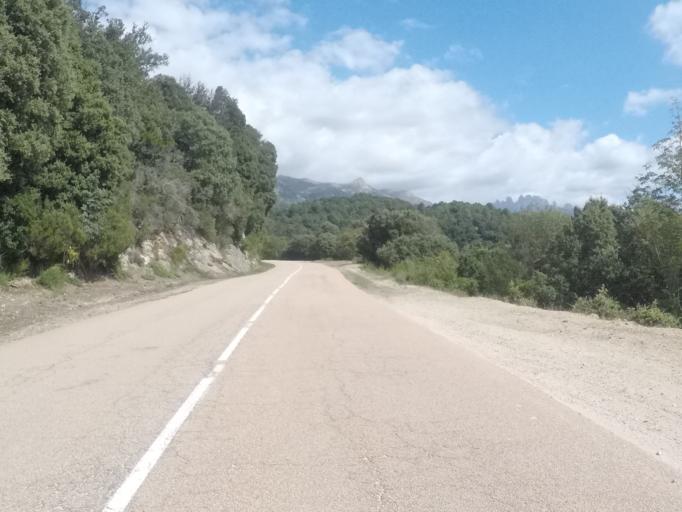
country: FR
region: Corsica
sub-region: Departement de la Corse-du-Sud
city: Zonza
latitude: 41.7583
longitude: 9.1271
